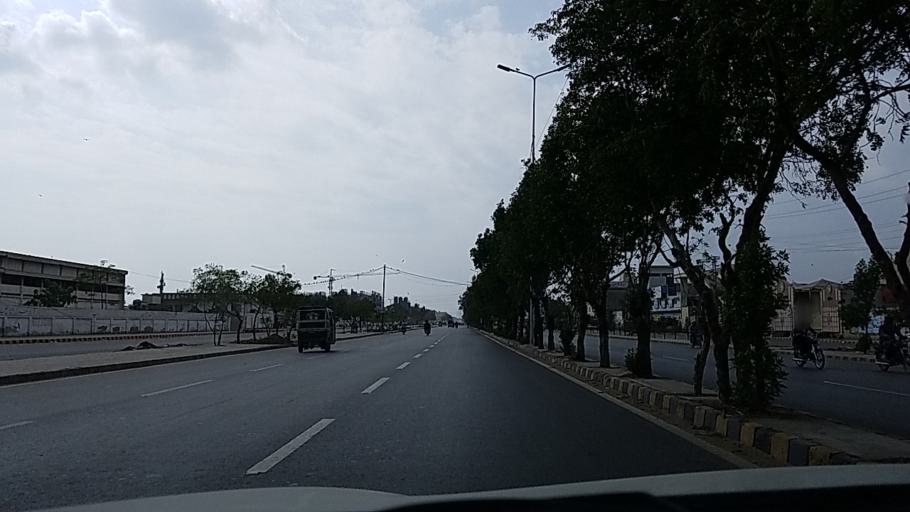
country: PK
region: Sindh
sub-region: Karachi District
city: Karachi
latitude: 24.8189
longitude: 67.1175
